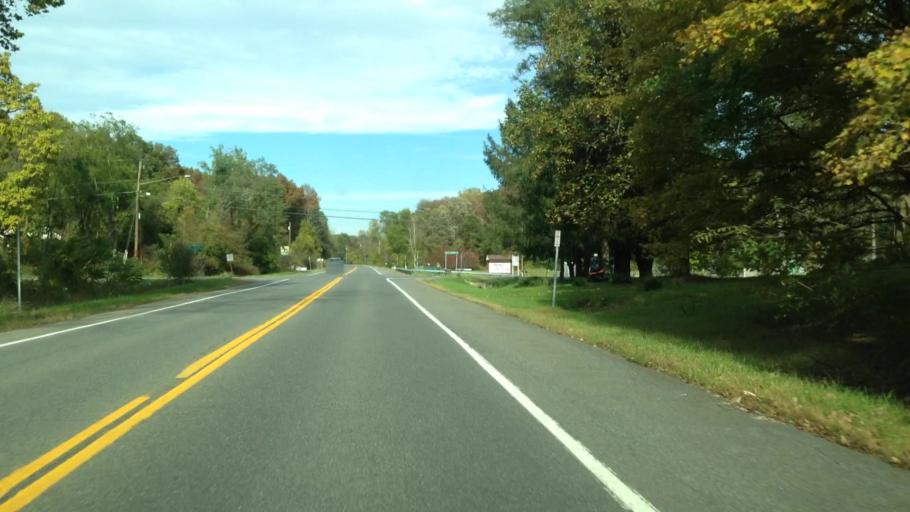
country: US
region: New York
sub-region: Ulster County
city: Port Ewen
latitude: 41.8804
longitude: -74.0207
